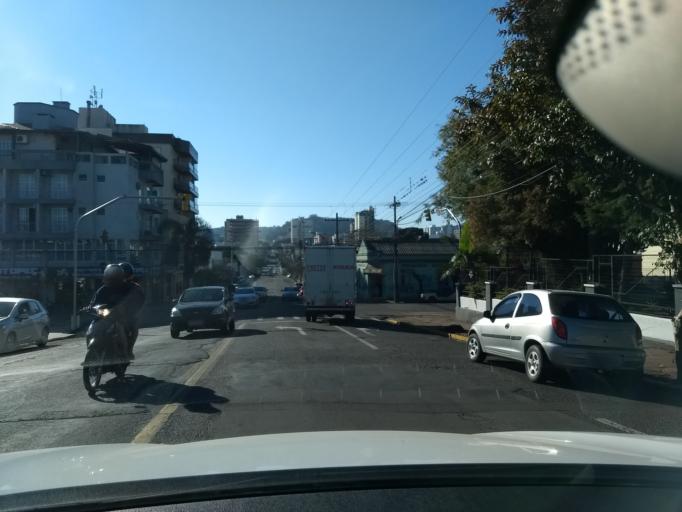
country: BR
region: Rio Grande do Sul
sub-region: Santa Cruz Do Sul
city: Santa Cruz do Sul
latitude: -29.7160
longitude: -52.4361
